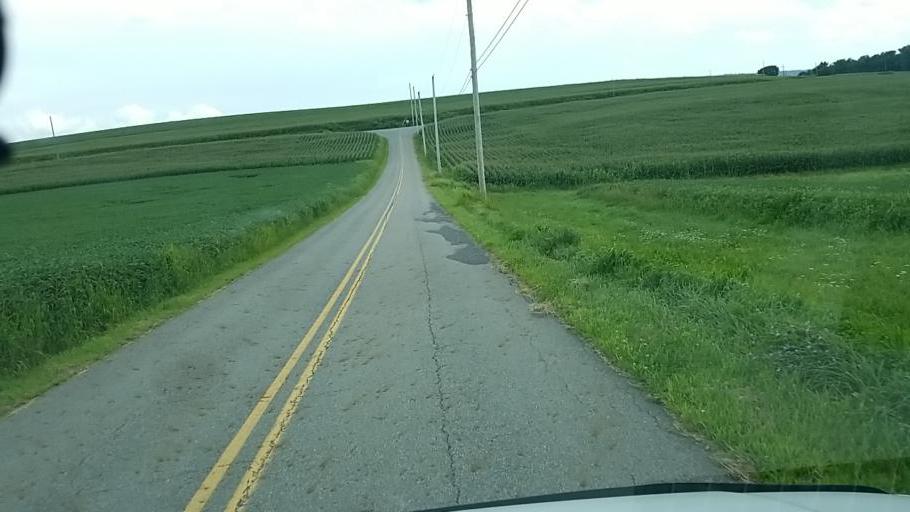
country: US
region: Pennsylvania
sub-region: Dauphin County
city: Elizabethville
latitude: 40.6505
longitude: -76.8350
